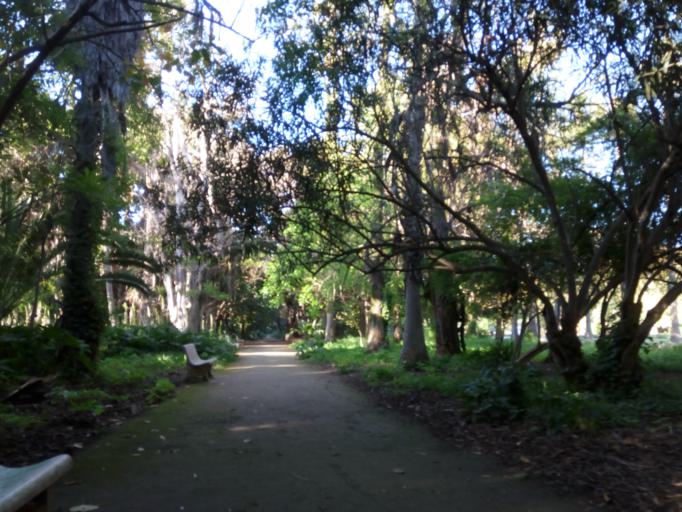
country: DZ
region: Alger
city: Algiers
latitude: 36.7495
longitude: 3.0739
